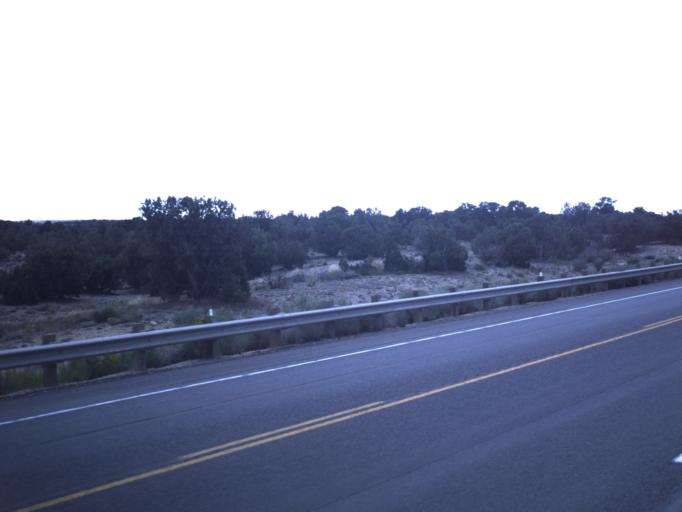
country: US
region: Utah
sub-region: Duchesne County
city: Duchesne
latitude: 40.1642
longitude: -110.4574
